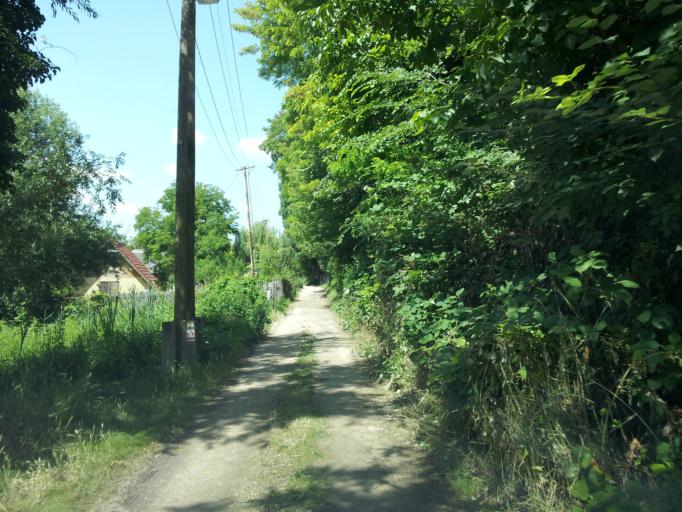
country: HU
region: Veszprem
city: Balatonkenese
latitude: 47.0342
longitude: 18.1022
